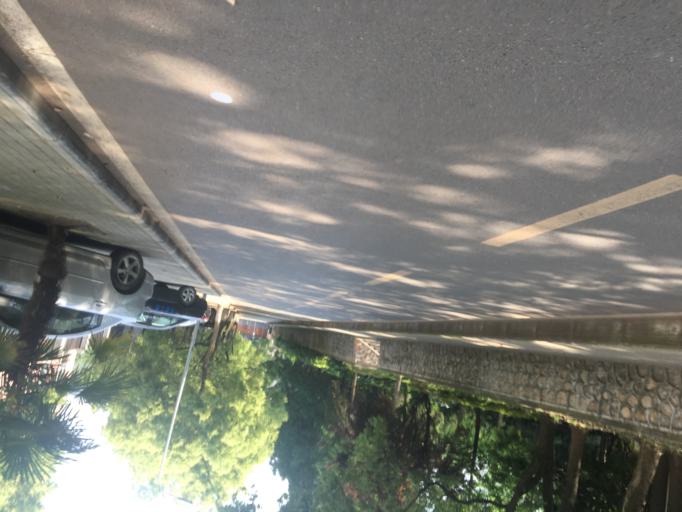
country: CN
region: Hubei
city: Guanshan
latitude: 30.5307
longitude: 114.3575
